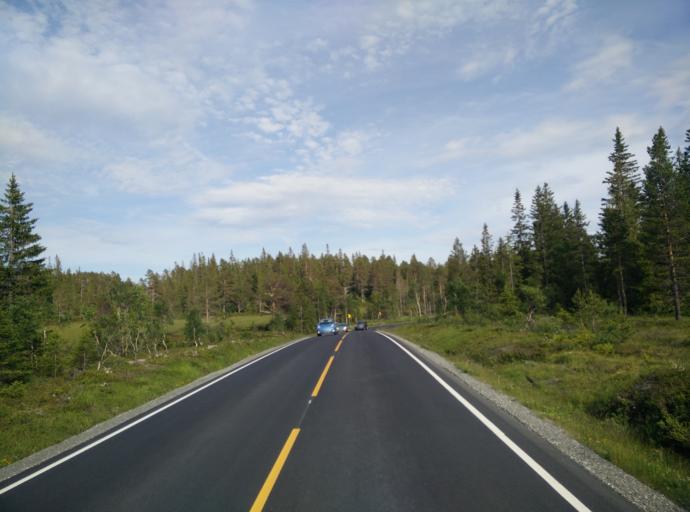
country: NO
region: Sor-Trondelag
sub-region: Snillfjord
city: Krokstadora
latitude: 63.2340
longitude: 9.5574
